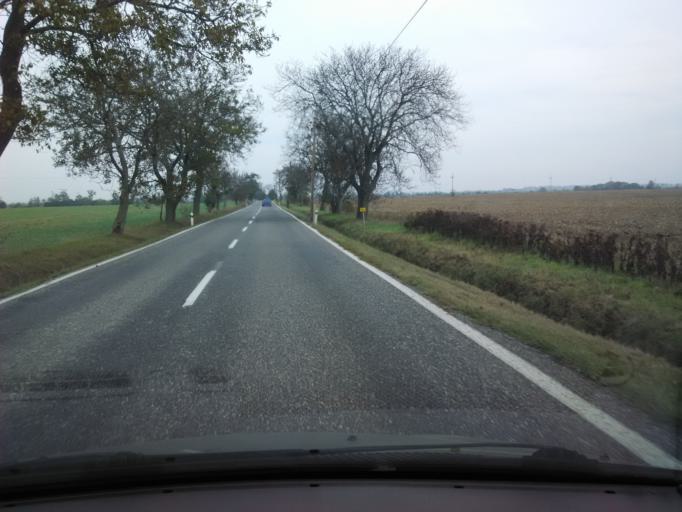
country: SK
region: Nitriansky
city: Zeliezovce
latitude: 48.0607
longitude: 18.5067
